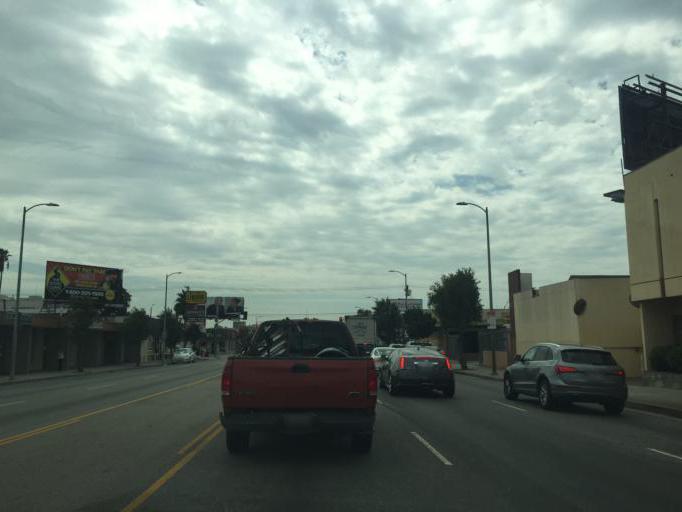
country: US
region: California
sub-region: Los Angeles County
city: Culver City
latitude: 34.0414
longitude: -118.3768
